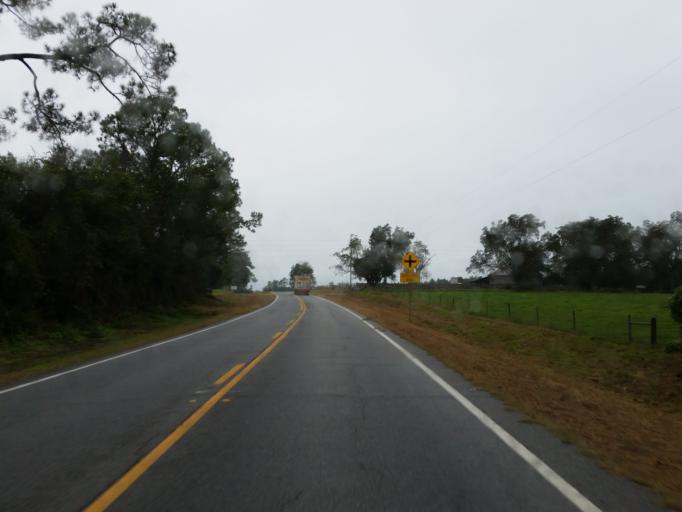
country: US
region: Georgia
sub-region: Berrien County
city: Nashville
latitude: 31.1164
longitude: -83.3084
